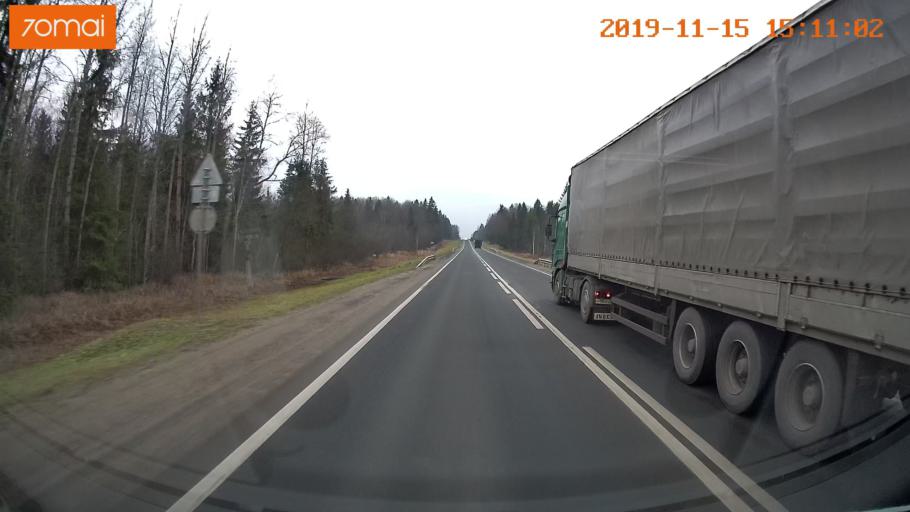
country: RU
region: Jaroslavl
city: Prechistoye
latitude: 58.3417
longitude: 40.2478
